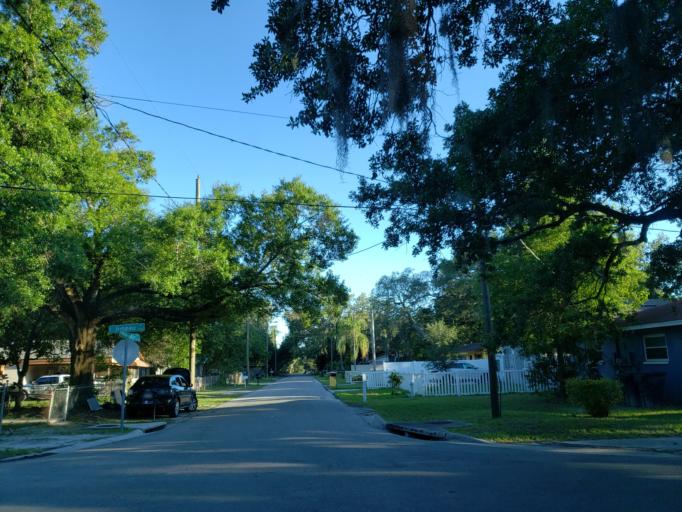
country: US
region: Florida
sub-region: Hillsborough County
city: University
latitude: 28.0240
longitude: -82.4384
